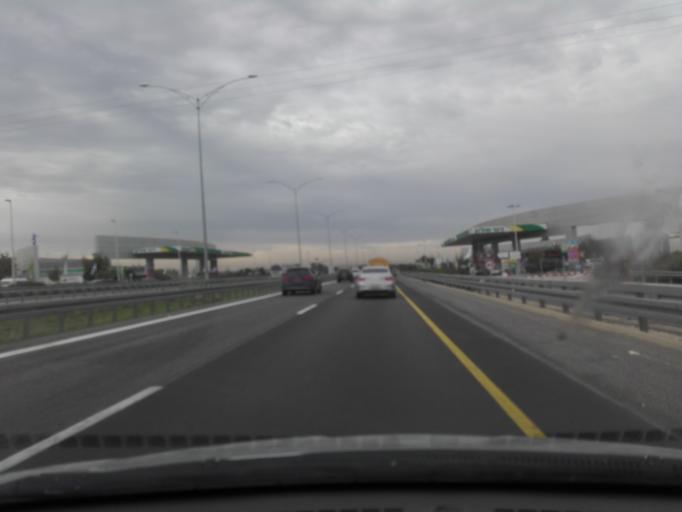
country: IL
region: Central District
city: Mazkeret Batya
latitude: 31.8834
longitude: 34.8794
